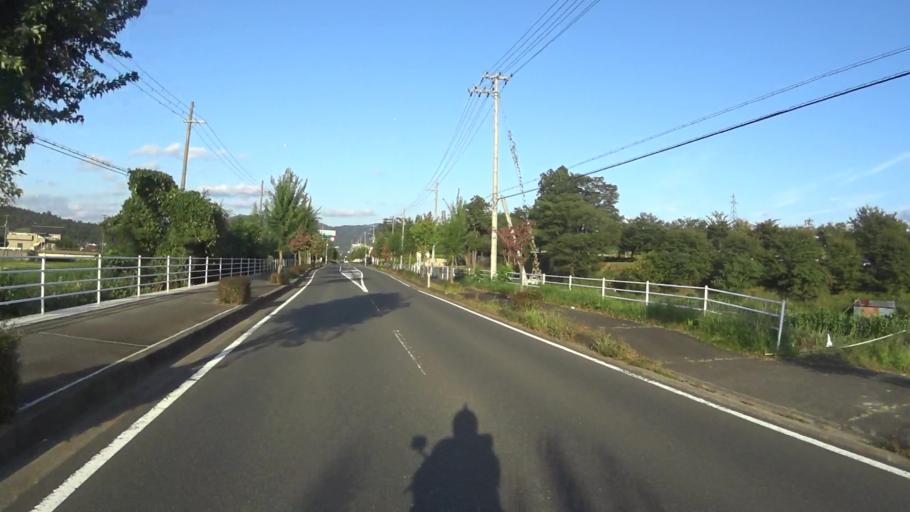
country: JP
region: Kyoto
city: Miyazu
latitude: 35.6066
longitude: 135.0567
